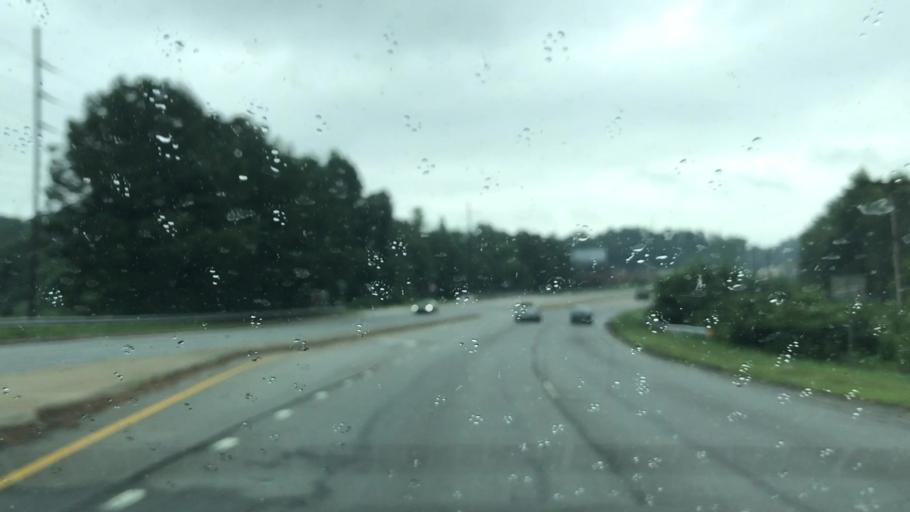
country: US
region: Georgia
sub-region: Gwinnett County
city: Lilburn
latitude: 33.9204
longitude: -84.1389
